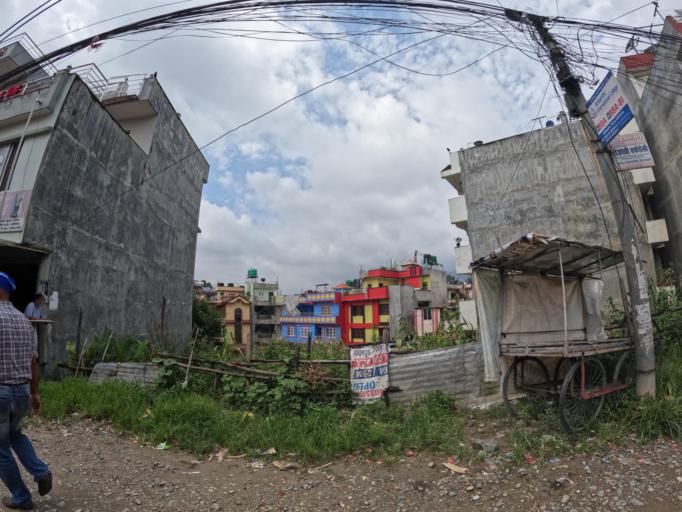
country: NP
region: Central Region
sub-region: Bagmati Zone
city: Kathmandu
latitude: 27.7544
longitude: 85.3180
